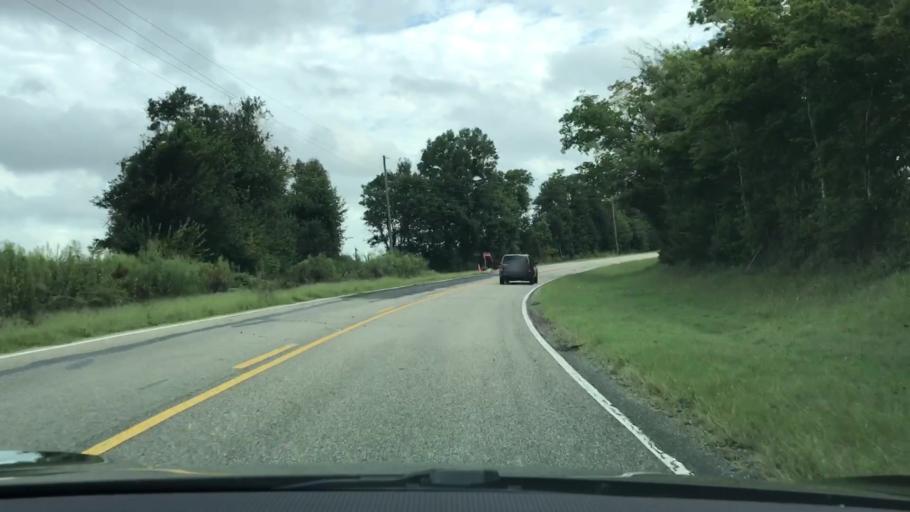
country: US
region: Alabama
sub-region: Montgomery County
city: Pike Road
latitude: 32.2992
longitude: -86.0727
